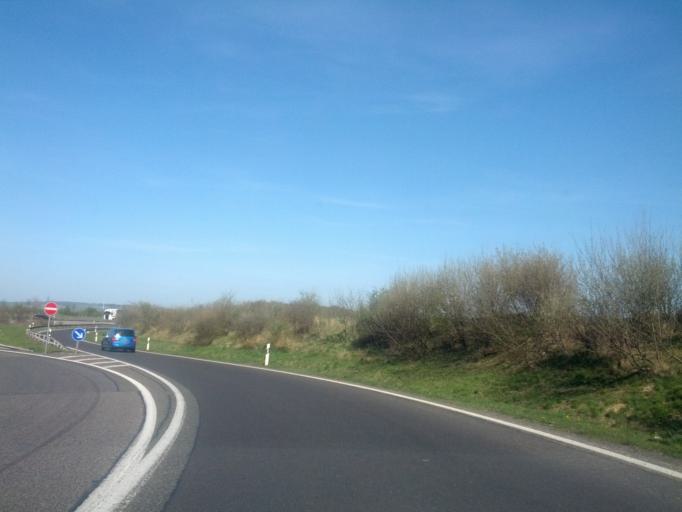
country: DE
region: Thuringia
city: Waltershausen
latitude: 50.9188
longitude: 10.5498
